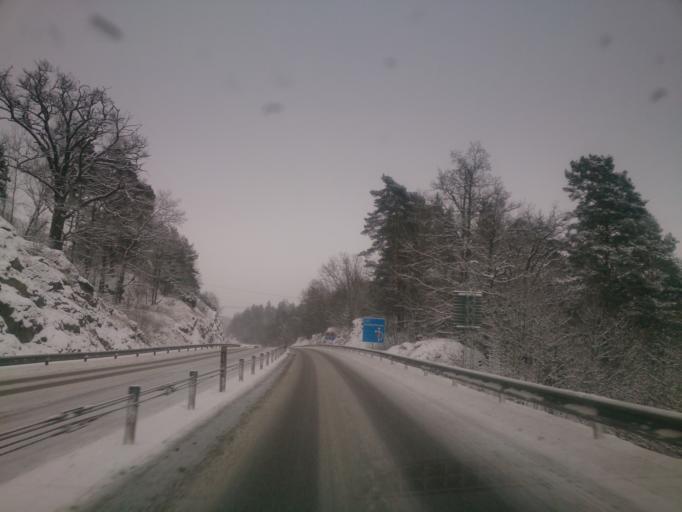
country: SE
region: OEstergoetland
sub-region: Norrkopings Kommun
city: Svartinge
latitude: 58.6953
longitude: 15.9088
